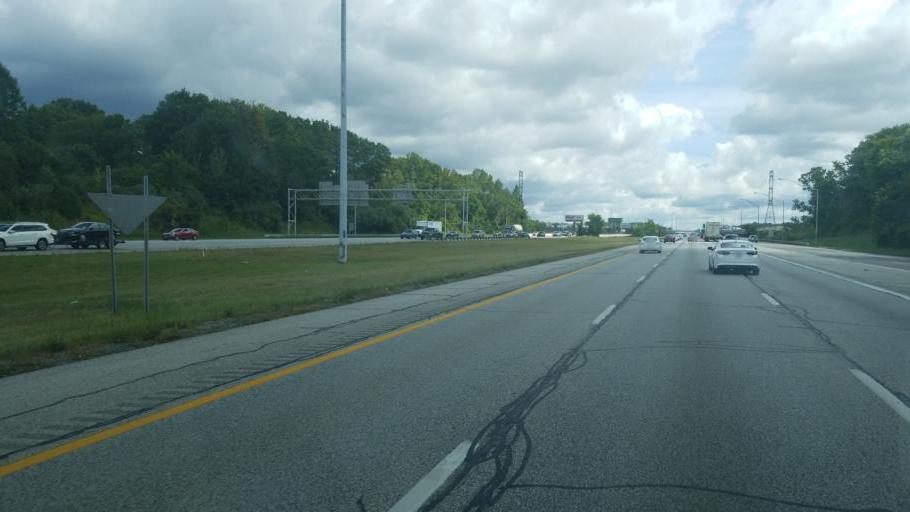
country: US
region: Ohio
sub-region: Cuyahoga County
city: Garfield Heights
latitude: 41.4072
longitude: -81.6402
